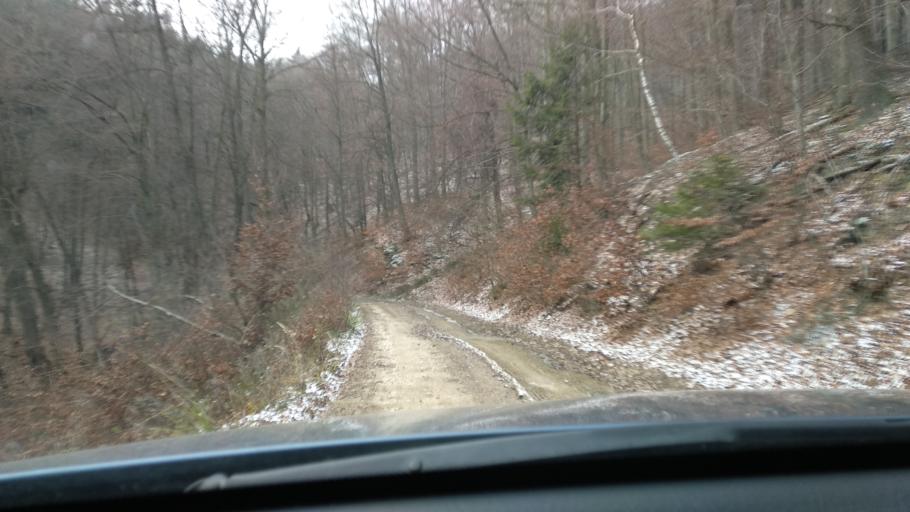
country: SK
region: Trenciansky
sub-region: Okres Trencin
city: Trencin
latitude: 48.7986
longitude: 18.0694
